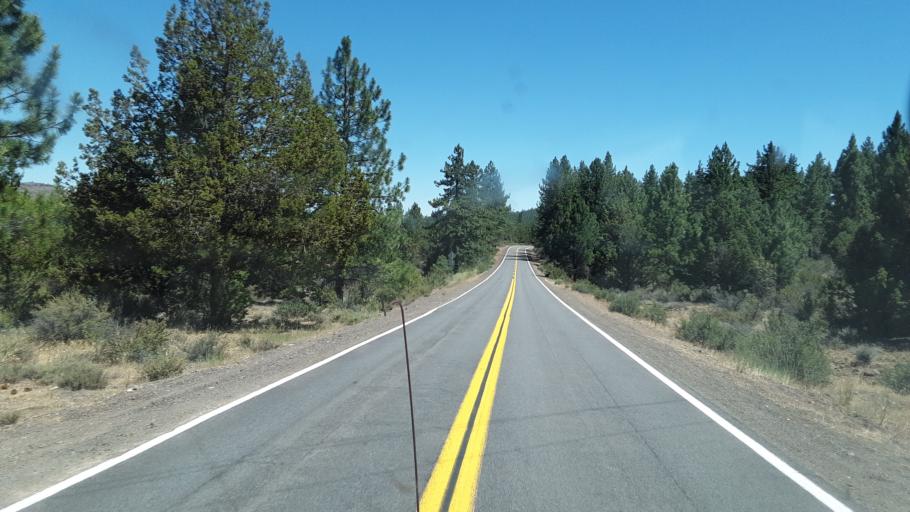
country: US
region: California
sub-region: Lassen County
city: Johnstonville
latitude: 40.5019
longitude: -120.5661
